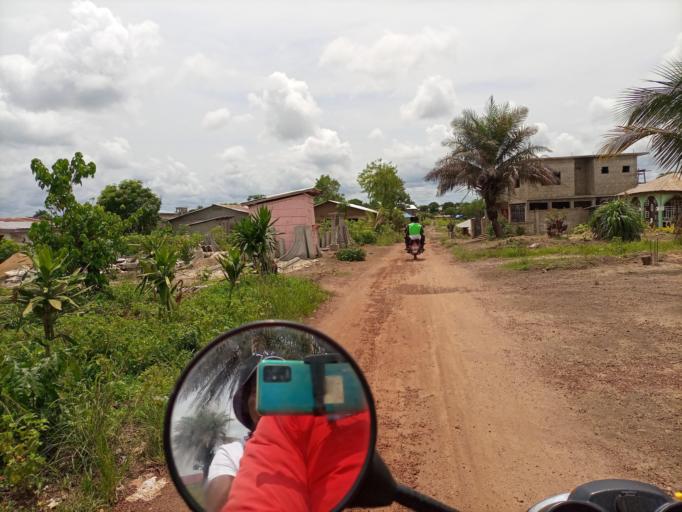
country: SL
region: Southern Province
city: Baoma
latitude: 7.9787
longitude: -11.7203
